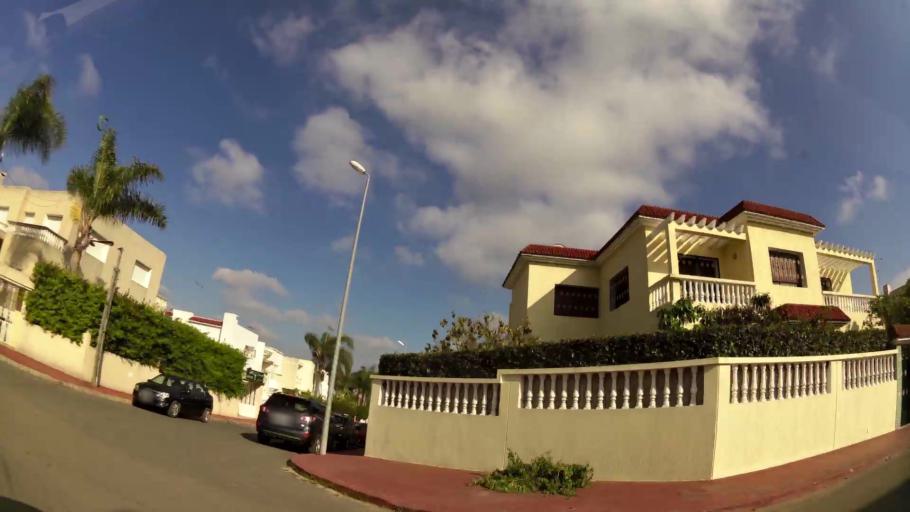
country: MA
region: Rabat-Sale-Zemmour-Zaer
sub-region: Skhirate-Temara
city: Temara
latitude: 33.9543
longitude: -6.8614
